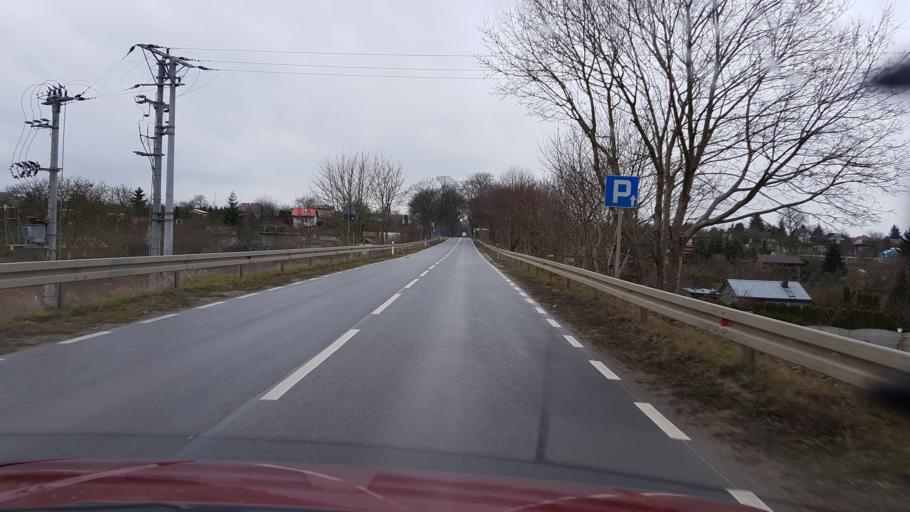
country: PL
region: West Pomeranian Voivodeship
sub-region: Powiat gryfinski
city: Gryfino
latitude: 53.2581
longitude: 14.5062
